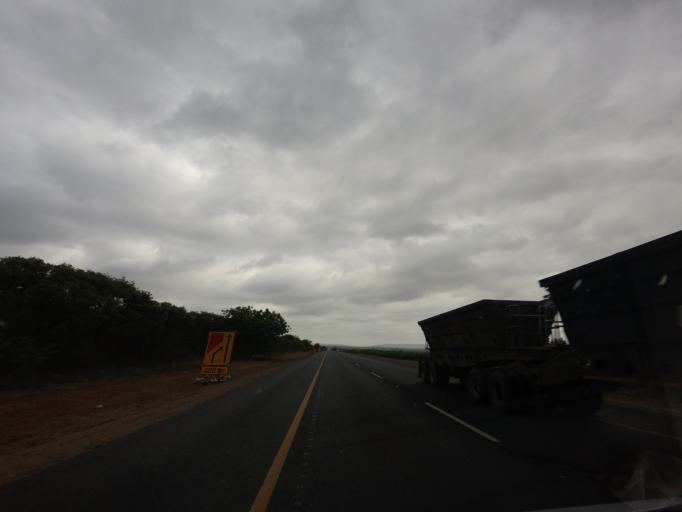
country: ZA
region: Mpumalanga
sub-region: Ehlanzeni District
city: Komatipoort
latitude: -25.4382
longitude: 31.7876
